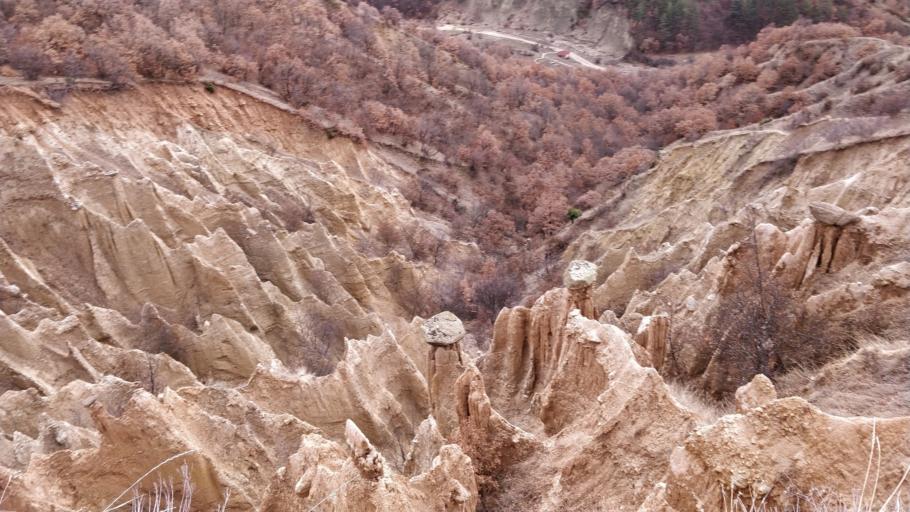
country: BG
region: Kyustendil
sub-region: Obshtina Rila
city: Rila
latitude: 42.0929
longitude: 23.1185
